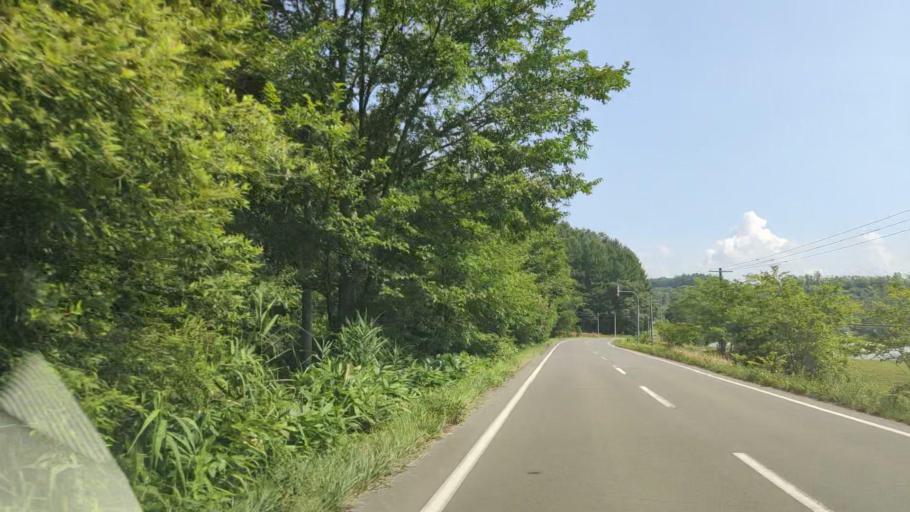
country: JP
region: Hokkaido
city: Shimo-furano
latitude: 43.4295
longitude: 142.4072
